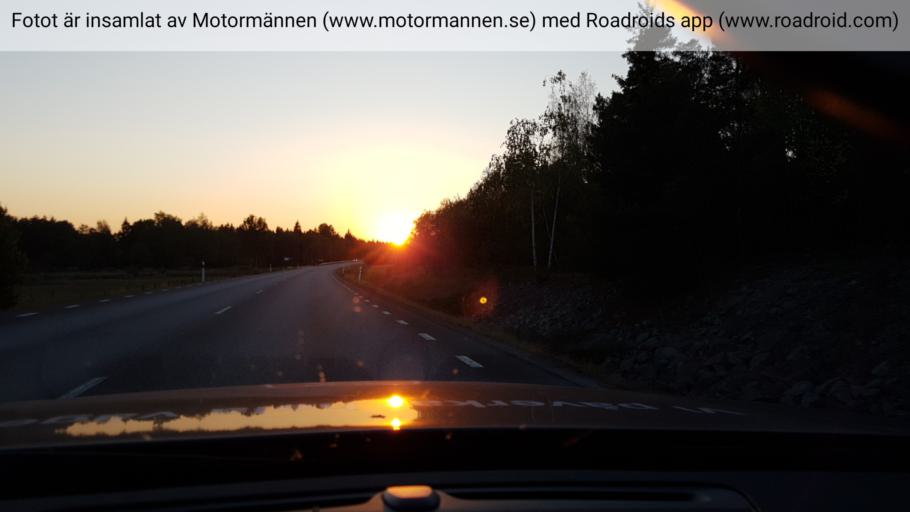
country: SE
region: Uppsala
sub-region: Osthammars Kommun
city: Bjorklinge
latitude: 59.9783
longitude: 17.3454
